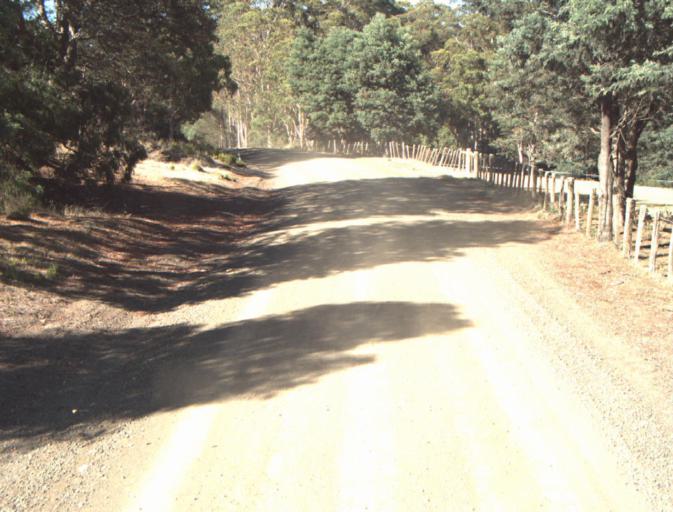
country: AU
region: Tasmania
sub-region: Launceston
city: Newstead
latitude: -41.2987
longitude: 147.3353
